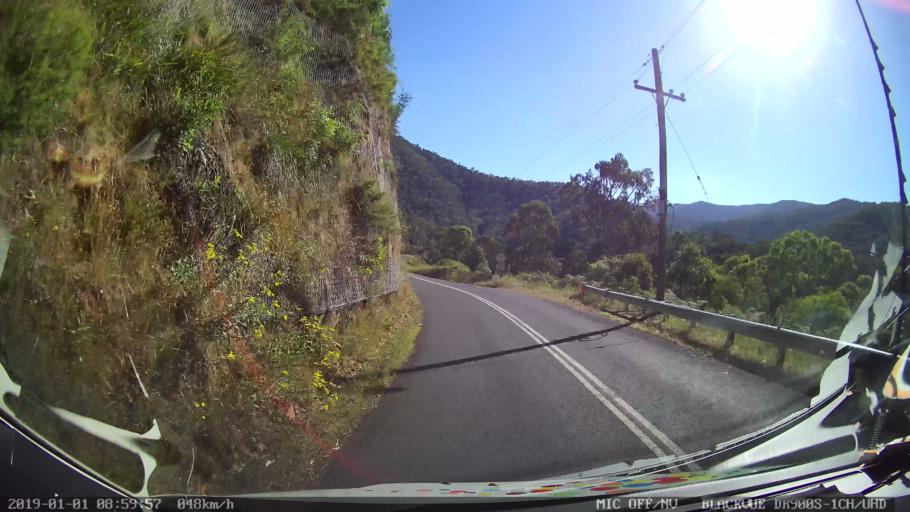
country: AU
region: New South Wales
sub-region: Snowy River
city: Jindabyne
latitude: -36.2381
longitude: 148.1803
